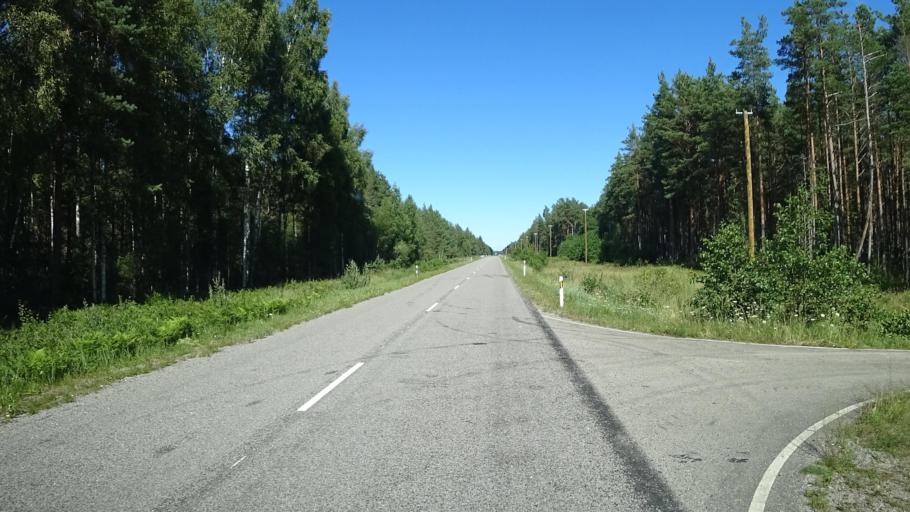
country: LV
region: Dundaga
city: Dundaga
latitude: 57.5973
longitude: 22.0309
